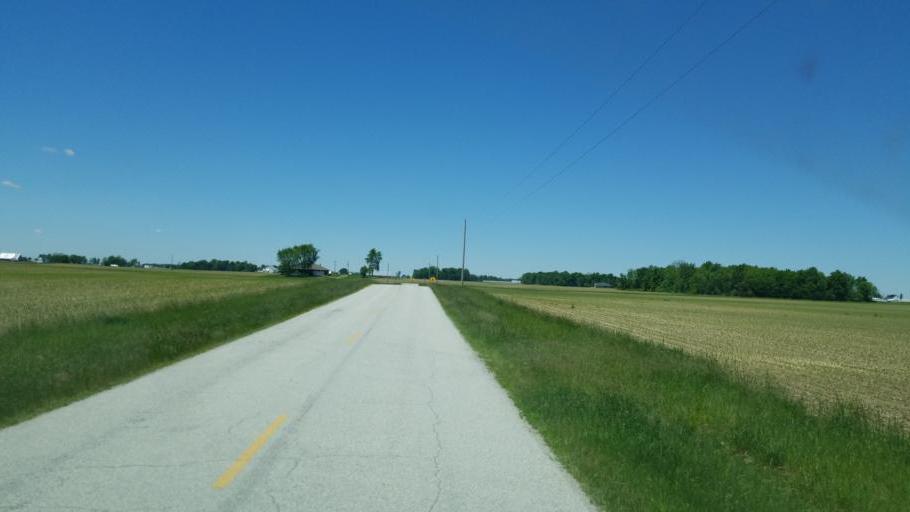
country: US
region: Ohio
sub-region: Auglaize County
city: Minster
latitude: 40.3856
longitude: -84.4519
